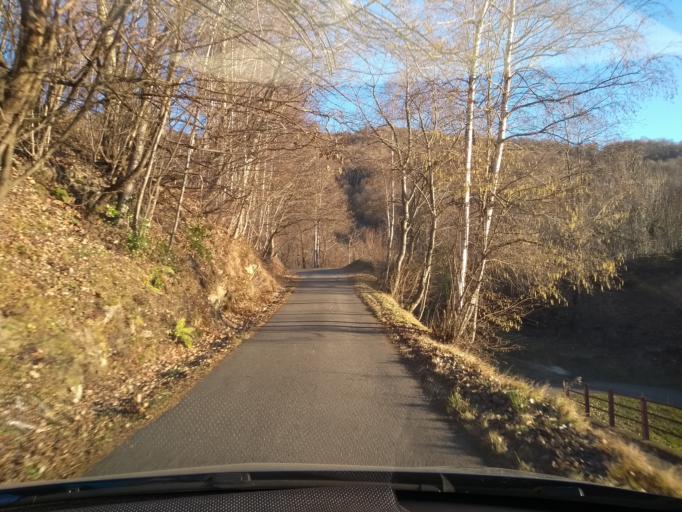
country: IT
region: Piedmont
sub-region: Provincia di Torino
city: Corio
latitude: 45.3219
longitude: 7.5380
